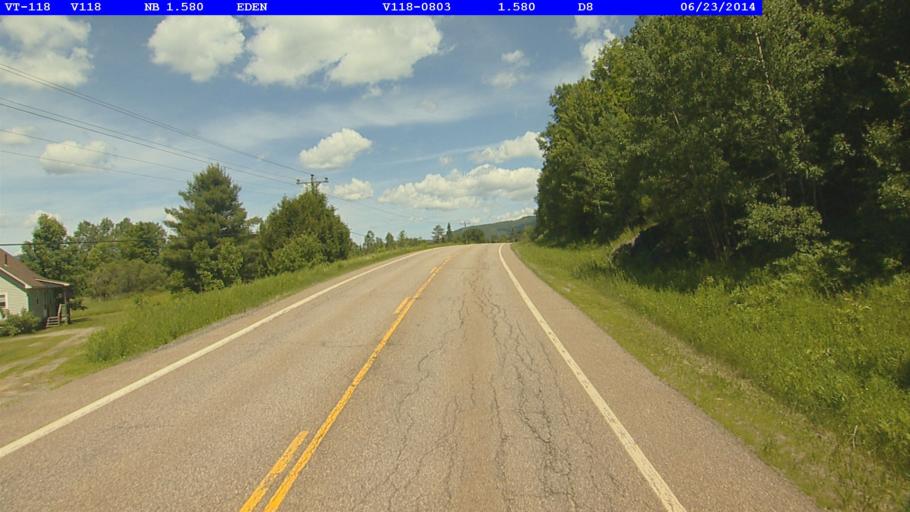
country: US
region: Vermont
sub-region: Lamoille County
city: Hyde Park
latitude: 44.7269
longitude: -72.5617
